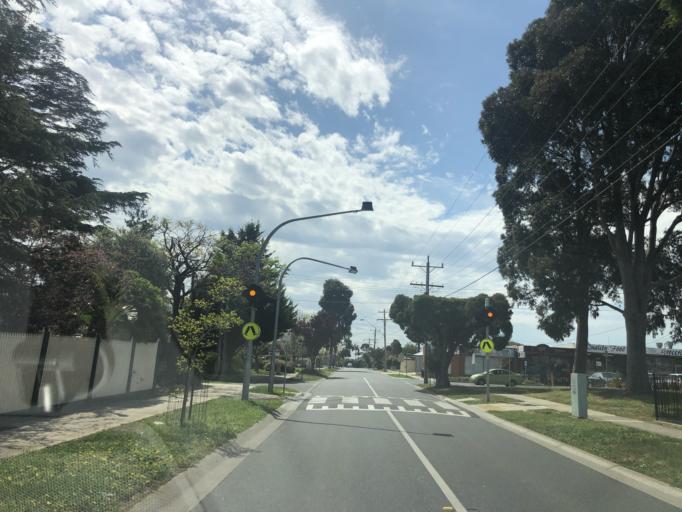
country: AU
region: Victoria
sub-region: Casey
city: Hallam
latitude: -38.0044
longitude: 145.2655
